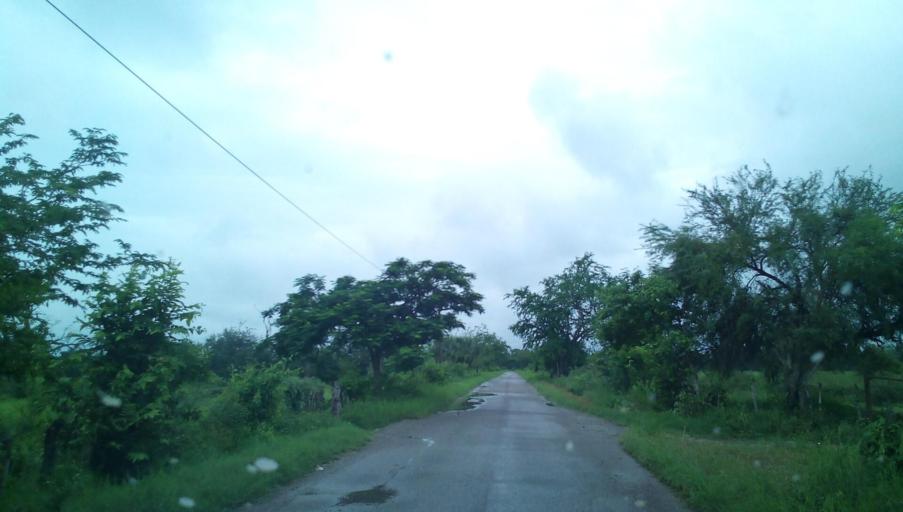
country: MX
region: Veracruz
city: Tempoal de Sanchez
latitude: 21.4785
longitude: -98.4192
